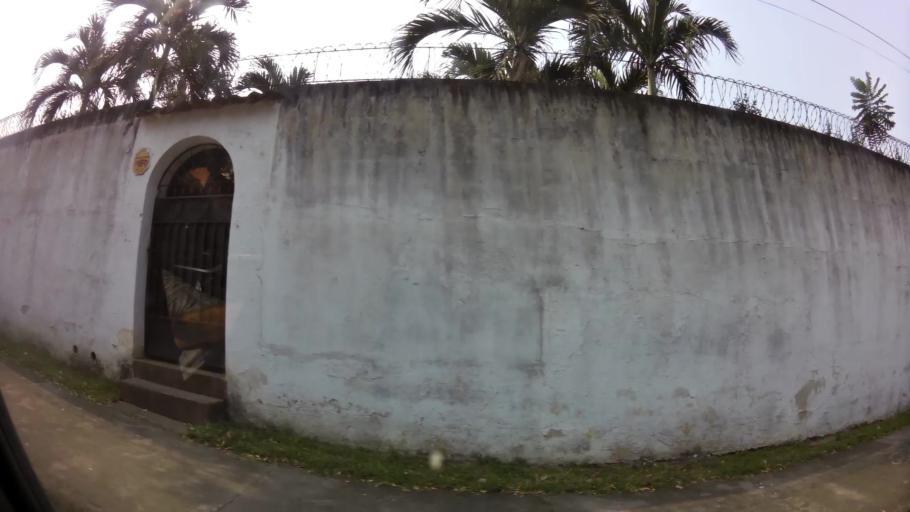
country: HN
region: Cortes
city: Armenta
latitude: 15.4952
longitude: -88.0410
